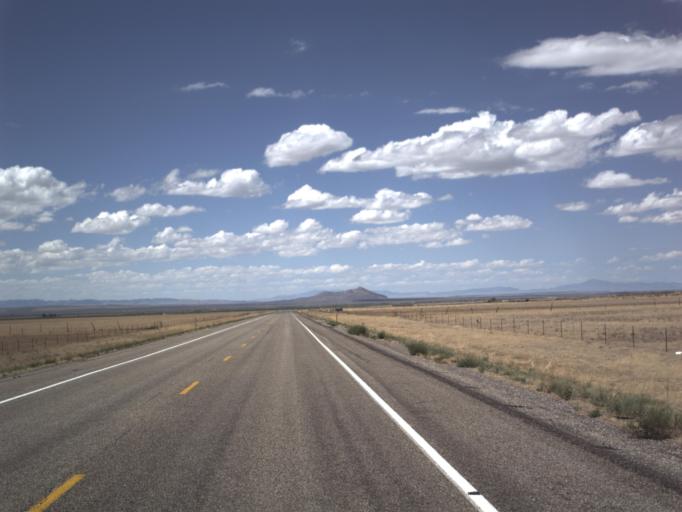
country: US
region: Utah
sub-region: Millard County
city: Fillmore
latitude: 39.1144
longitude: -112.2926
